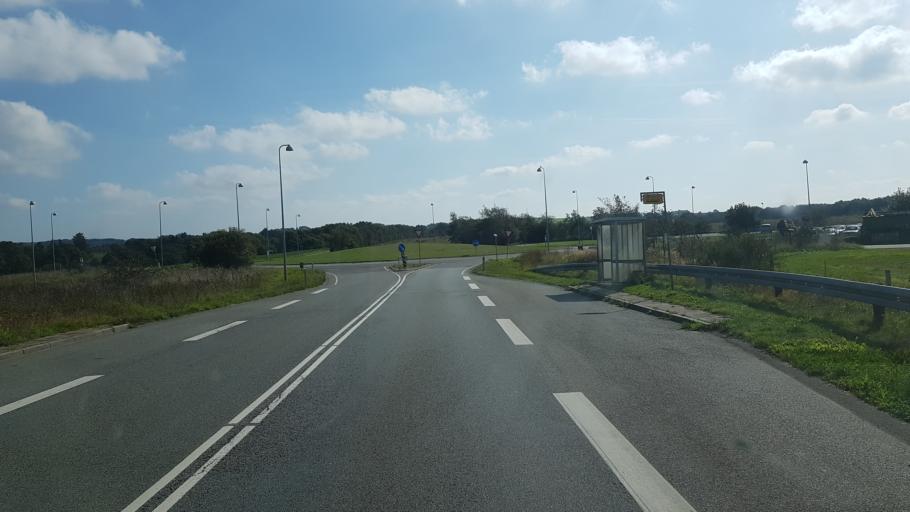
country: DK
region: South Denmark
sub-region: Kolding Kommune
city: Lunderskov
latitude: 55.5062
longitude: 9.3249
